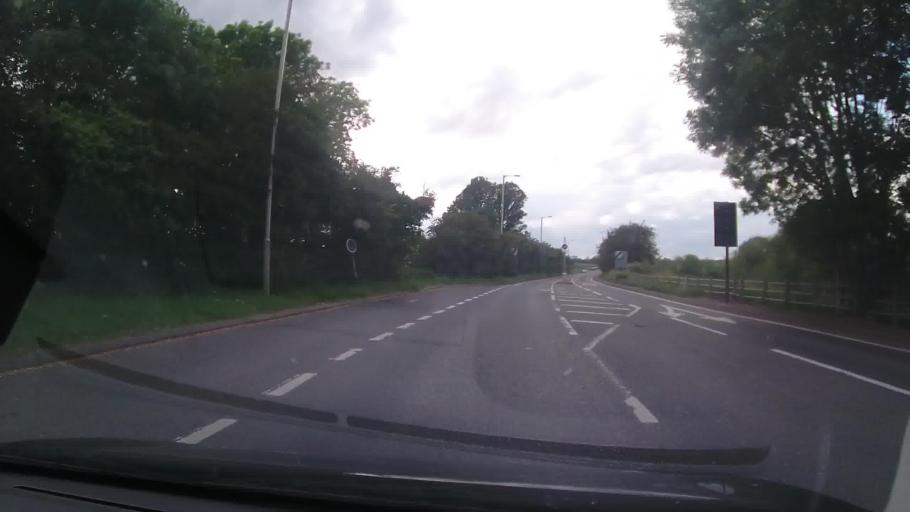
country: GB
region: England
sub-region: Shropshire
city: Berrington
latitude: 52.6794
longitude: -2.6826
